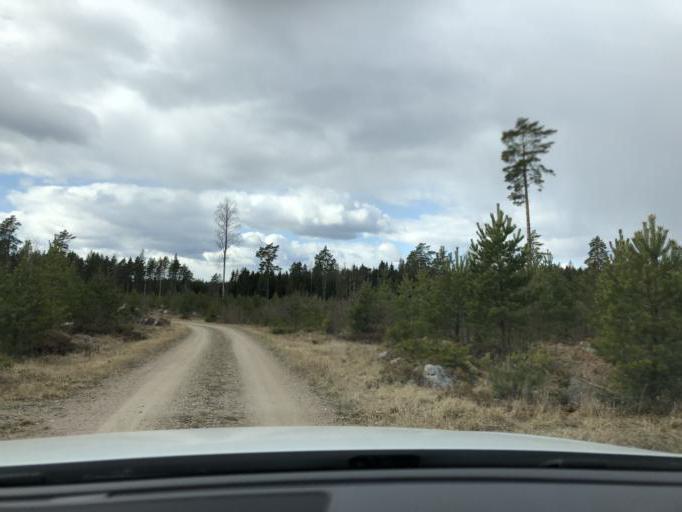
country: SE
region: Gaevleborg
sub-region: Gavle Kommun
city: Hedesunda
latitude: 60.3436
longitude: 17.0931
